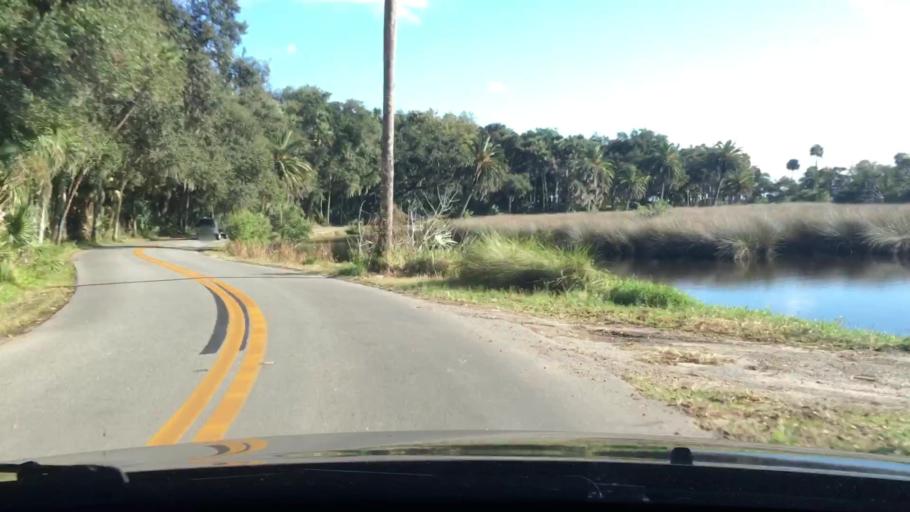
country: US
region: Florida
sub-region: Flagler County
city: Flagler Beach
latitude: 29.4036
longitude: -81.1151
